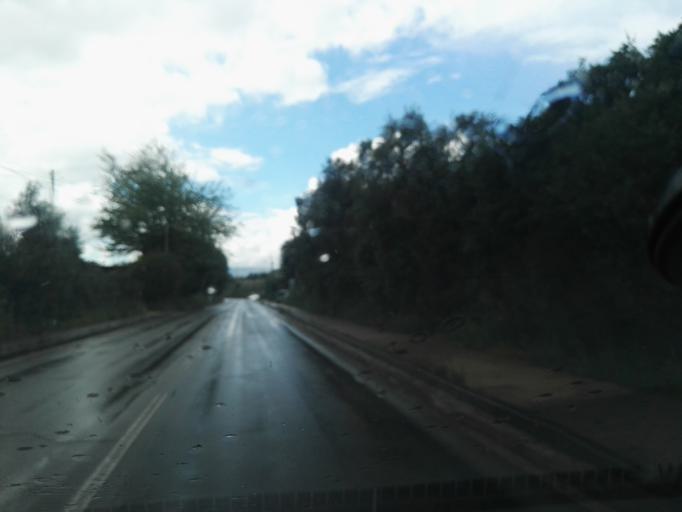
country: PT
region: Santarem
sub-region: Golega
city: Golega
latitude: 39.4122
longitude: -8.4910
